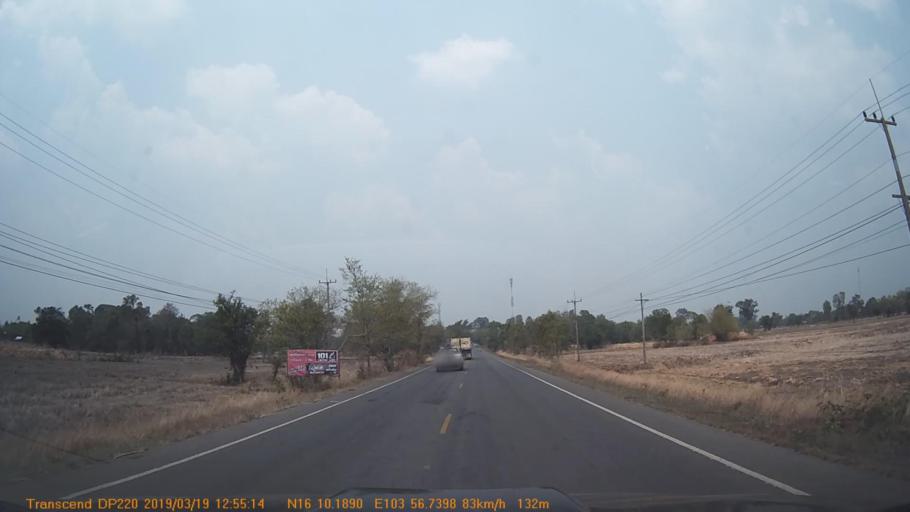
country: TH
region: Roi Et
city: Waeng
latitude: 16.1701
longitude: 103.9457
